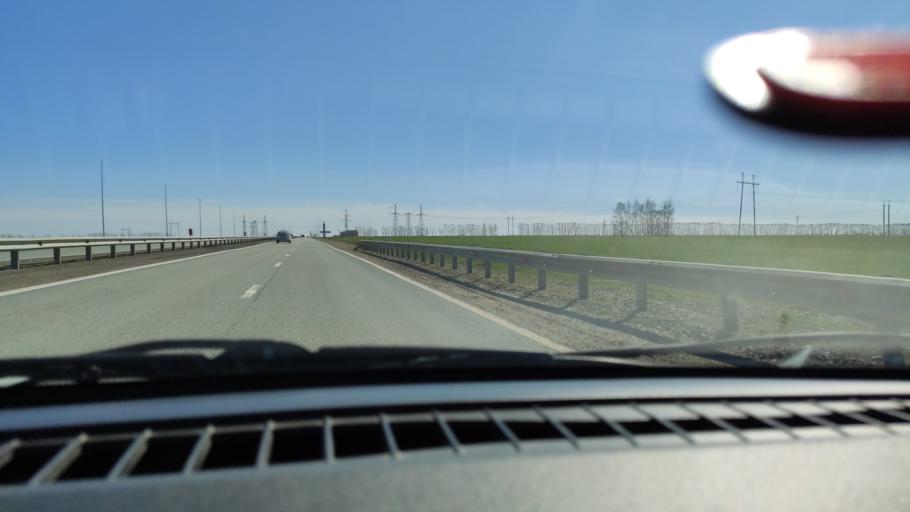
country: RU
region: Bashkortostan
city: Tolbazy
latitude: 54.2574
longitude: 55.8815
